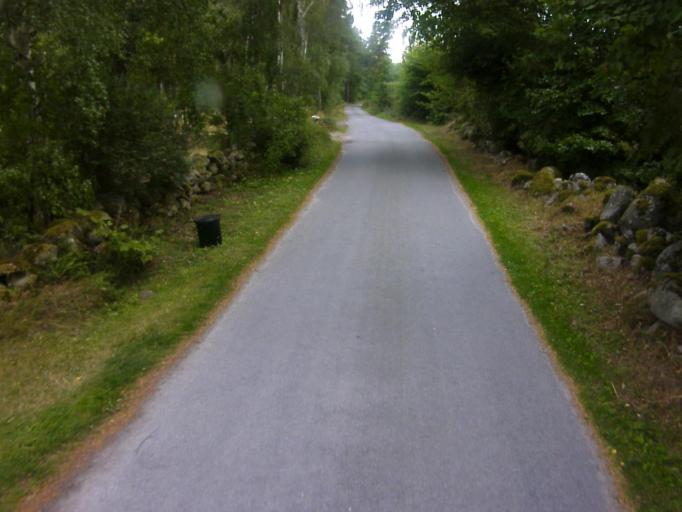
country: SE
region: Blekinge
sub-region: Solvesborgs Kommun
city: Soelvesborg
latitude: 56.0077
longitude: 14.6271
